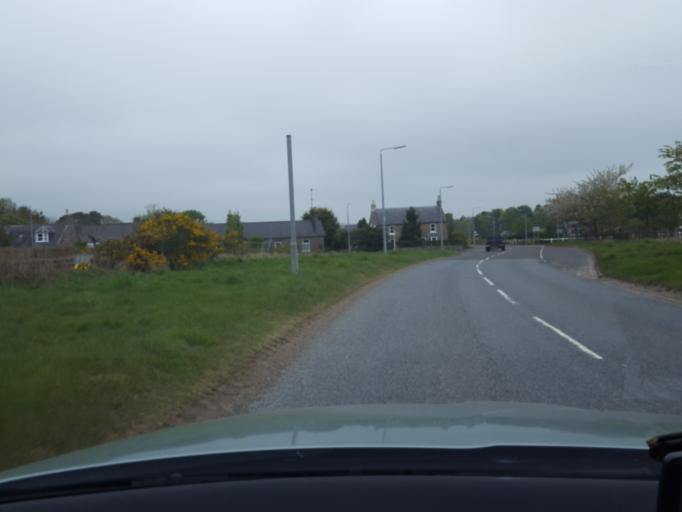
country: GB
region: Scotland
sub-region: Angus
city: Brechin
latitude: 56.7782
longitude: -2.6448
